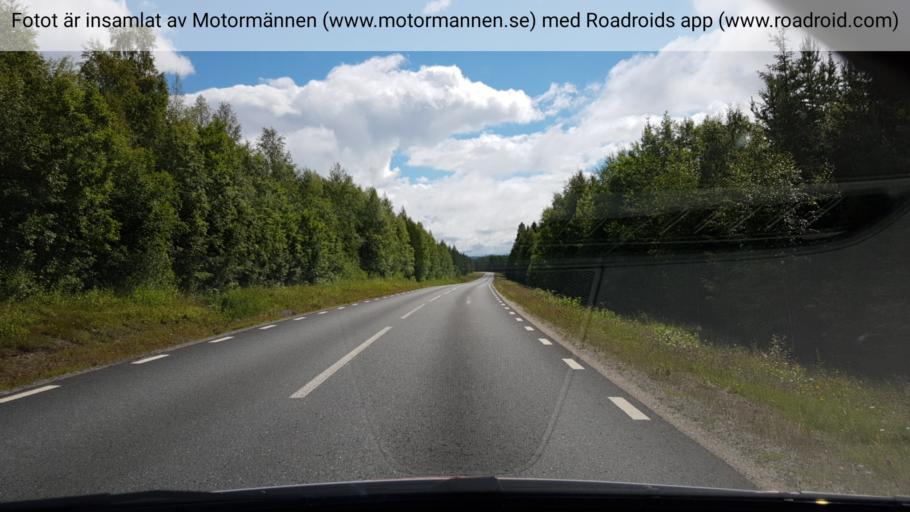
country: SE
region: Vaesterbotten
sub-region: Bjurholms Kommun
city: Bjurholm
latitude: 64.3230
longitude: 19.1573
